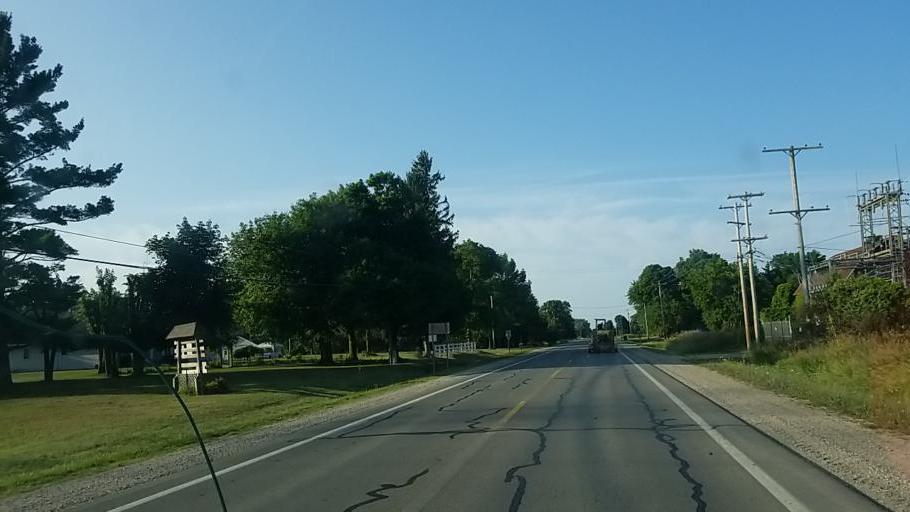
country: US
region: Michigan
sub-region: Montcalm County
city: Stanton
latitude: 43.2040
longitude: -85.0737
